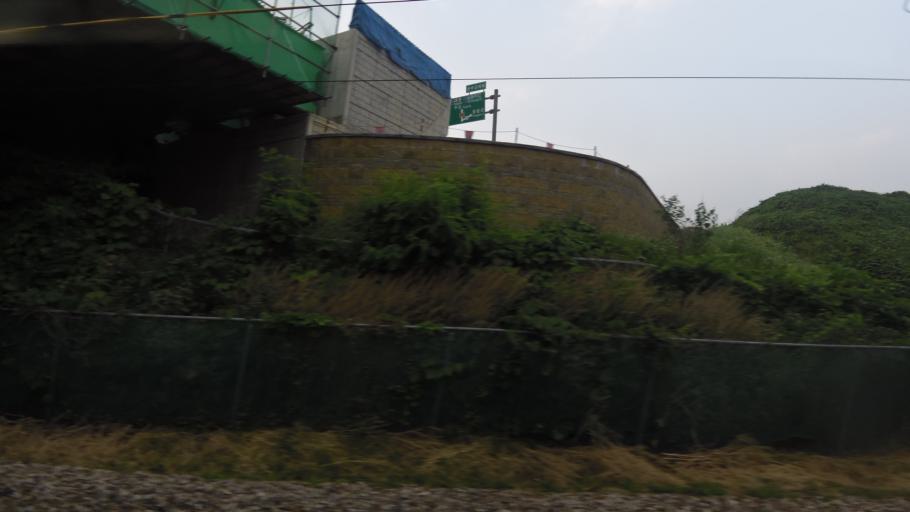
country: KR
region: Daejeon
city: Songgang-dong
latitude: 36.5388
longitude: 127.3416
